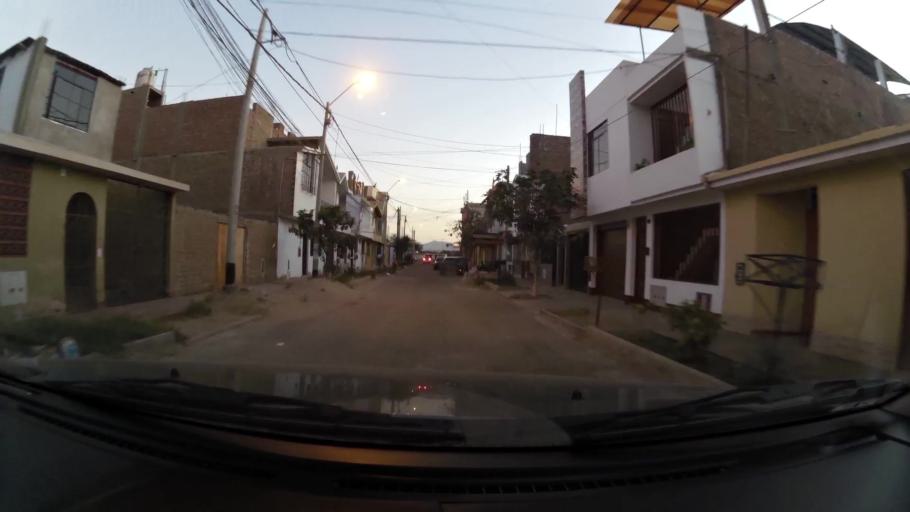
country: PE
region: Ica
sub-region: Provincia de Ica
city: Ica
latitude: -14.0849
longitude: -75.7292
